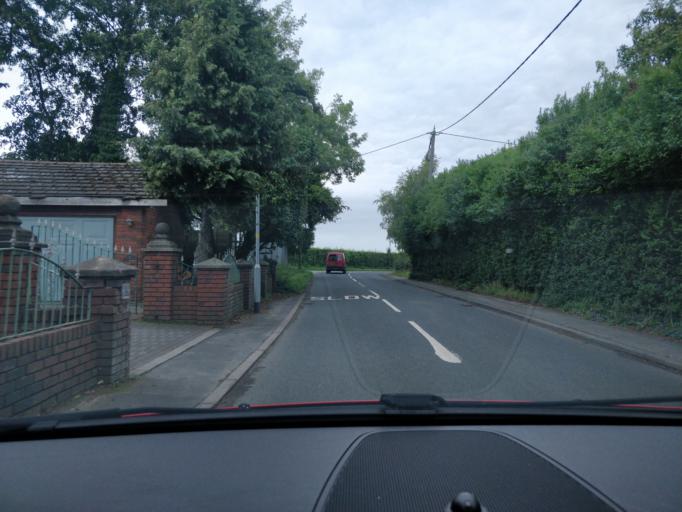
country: GB
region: England
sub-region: Lancashire
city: Ormskirk
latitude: 53.6034
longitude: -2.8655
